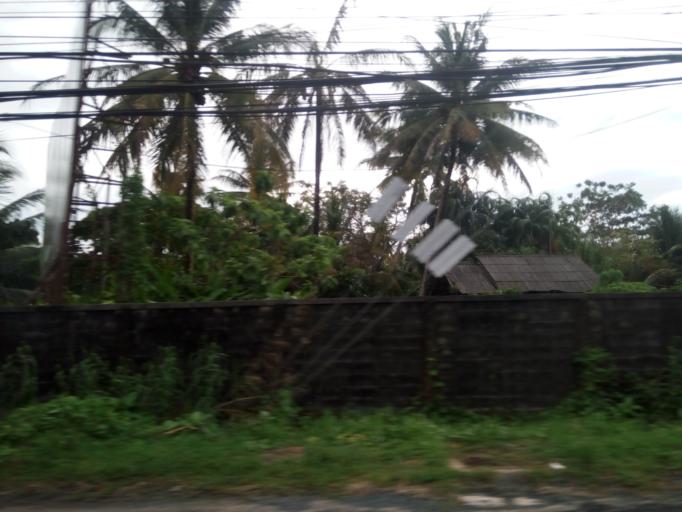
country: TH
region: Phuket
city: Thalang
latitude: 7.9923
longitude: 98.3537
